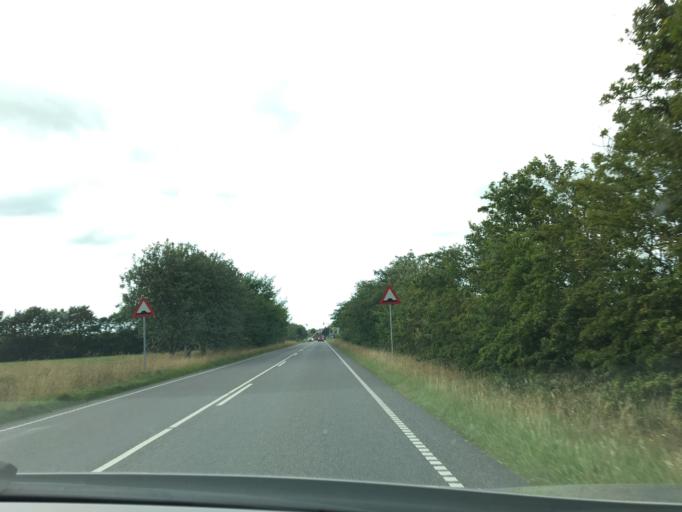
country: DK
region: South Denmark
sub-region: Varde Kommune
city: Oksbol
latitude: 55.7062
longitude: 8.3084
